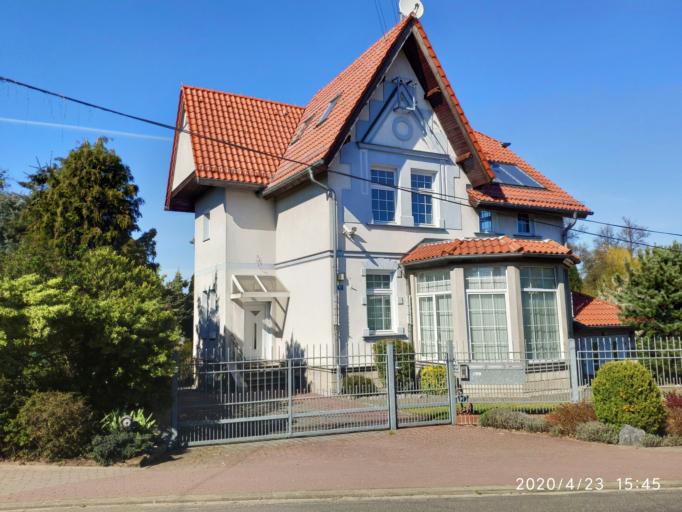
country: PL
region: Lubusz
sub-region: Powiat slubicki
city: Osno Lubuskie
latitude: 52.4594
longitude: 14.8675
